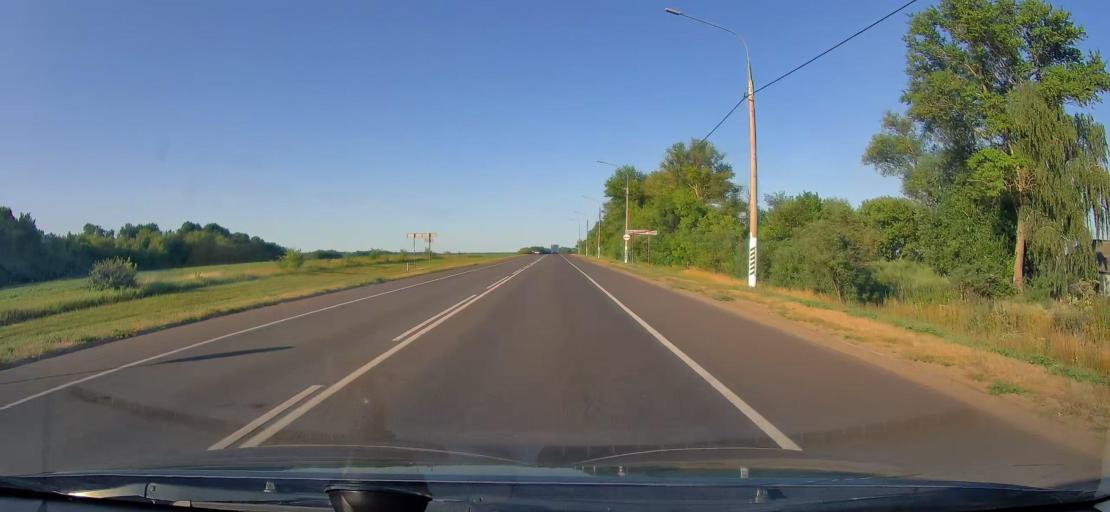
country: RU
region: Tula
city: Plavsk
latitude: 53.6475
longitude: 37.2226
